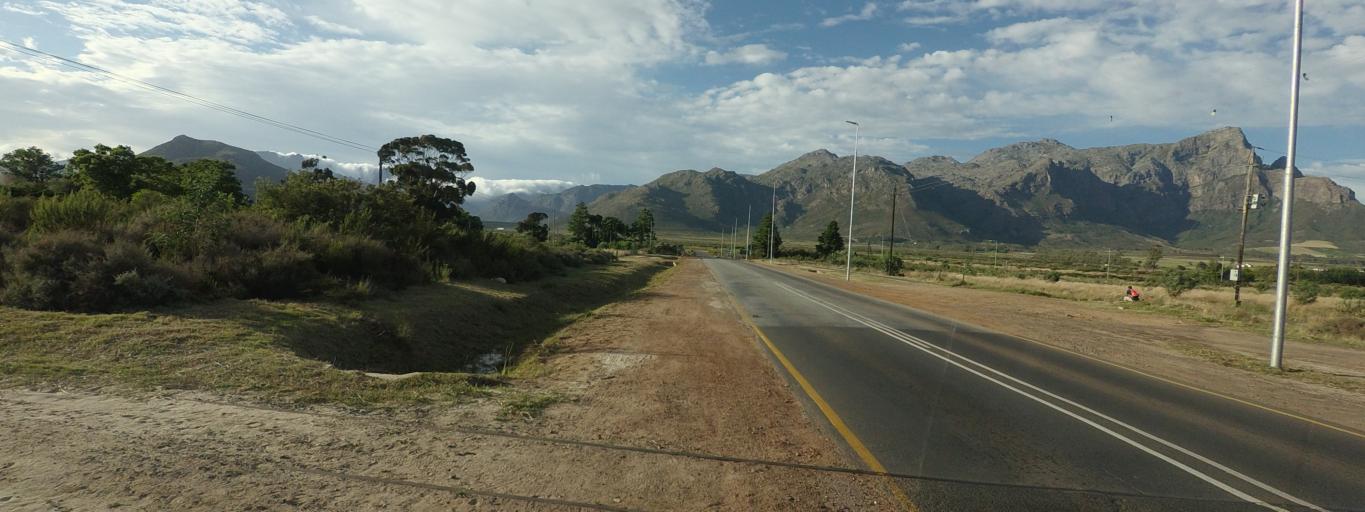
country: ZA
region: Western Cape
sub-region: Cape Winelands District Municipality
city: Paarl
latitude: -33.8764
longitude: 19.0446
